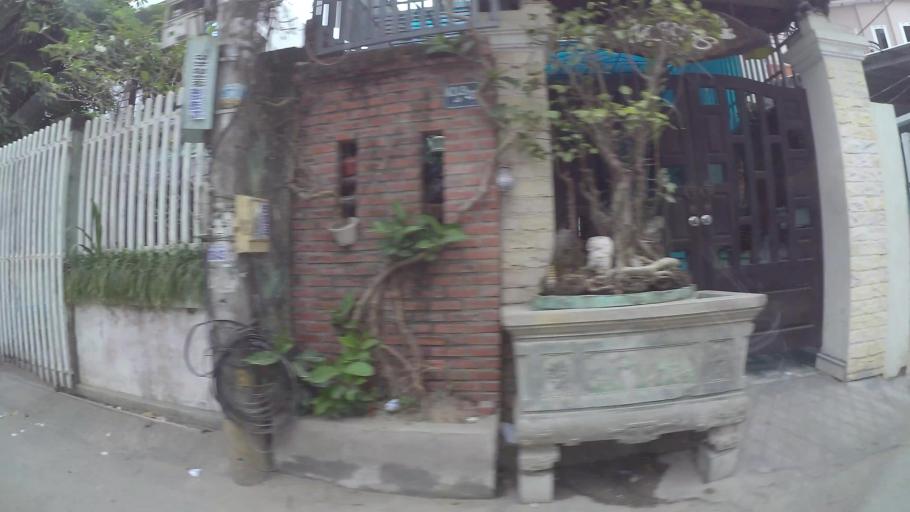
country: VN
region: Da Nang
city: Thanh Khe
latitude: 16.0591
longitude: 108.1890
